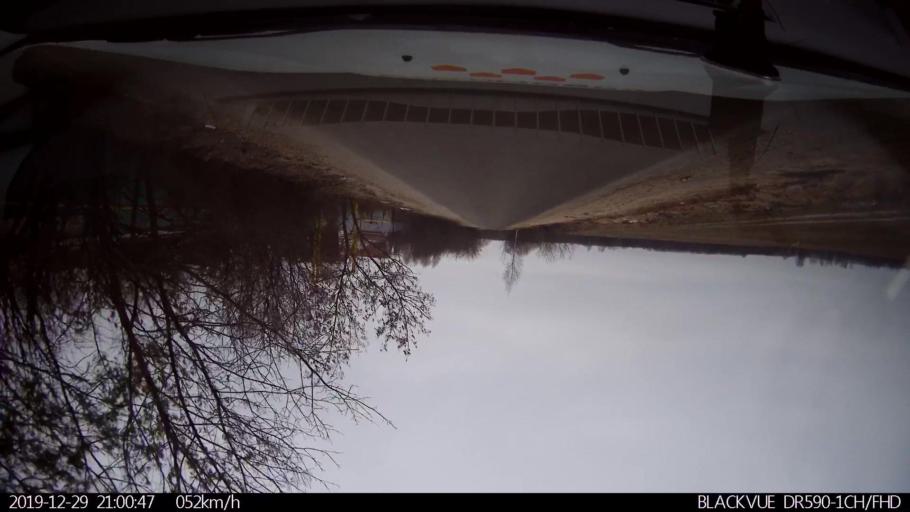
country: RU
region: Nizjnij Novgorod
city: Afonino
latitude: 56.1843
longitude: 43.9904
